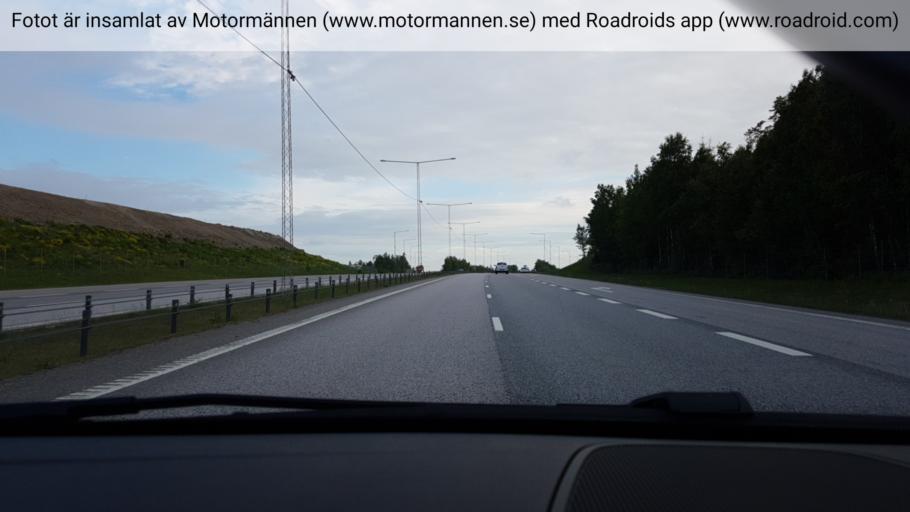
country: SE
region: Stockholm
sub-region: Haninge Kommun
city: Jordbro
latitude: 59.1126
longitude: 18.1268
